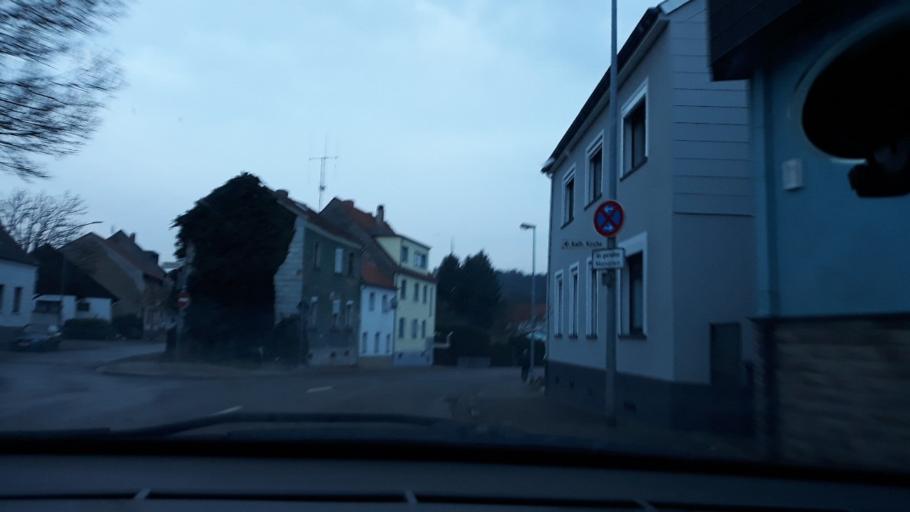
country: DE
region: Saarland
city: Sankt Ingbert
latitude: 49.2654
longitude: 7.1592
